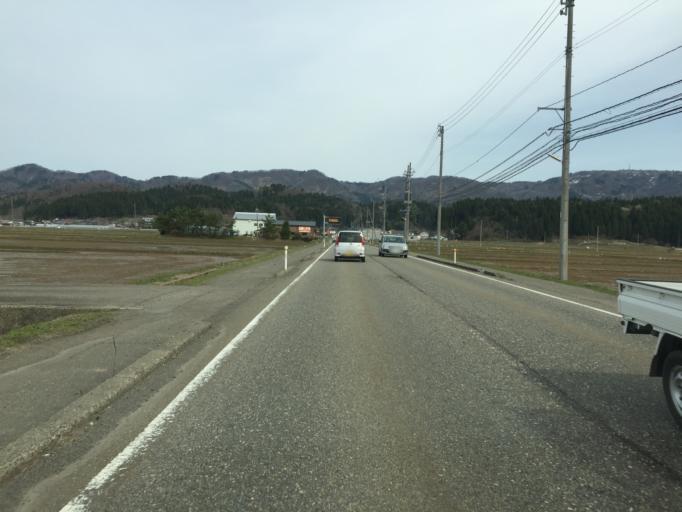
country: JP
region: Niigata
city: Nagaoka
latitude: 37.4543
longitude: 138.8908
